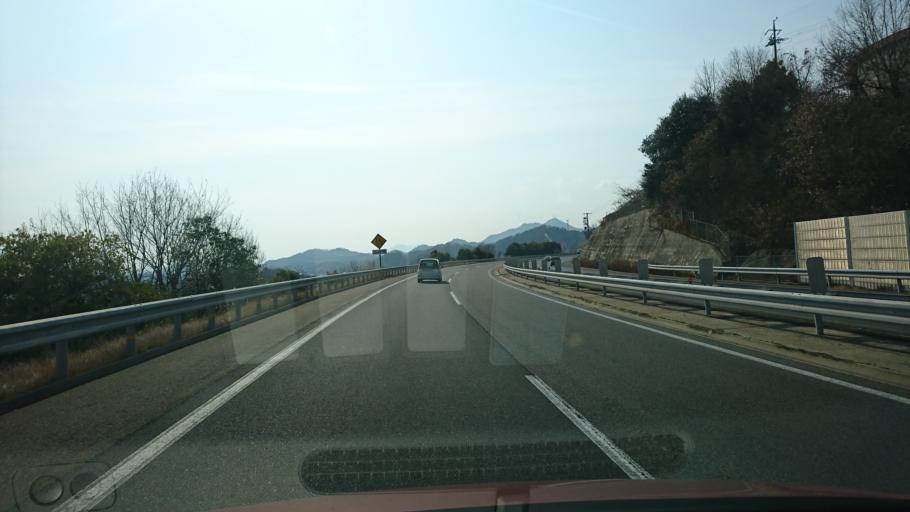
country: JP
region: Hiroshima
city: Onomichi
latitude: 34.4157
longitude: 133.2203
